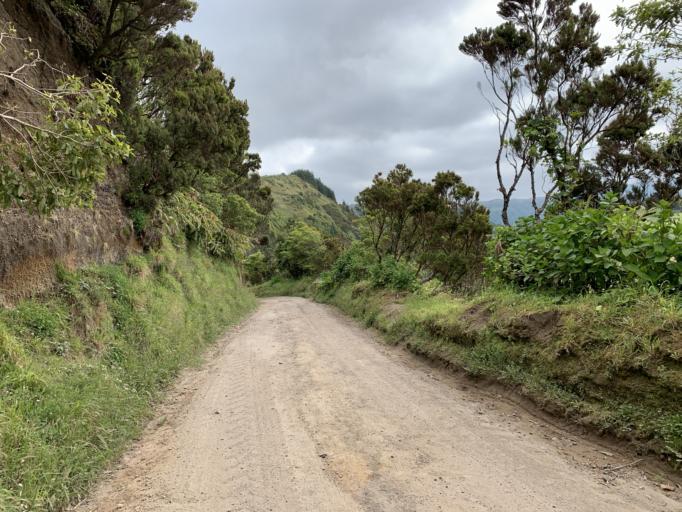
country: PT
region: Azores
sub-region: Ponta Delgada
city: Arrifes
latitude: 37.8719
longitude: -25.8122
